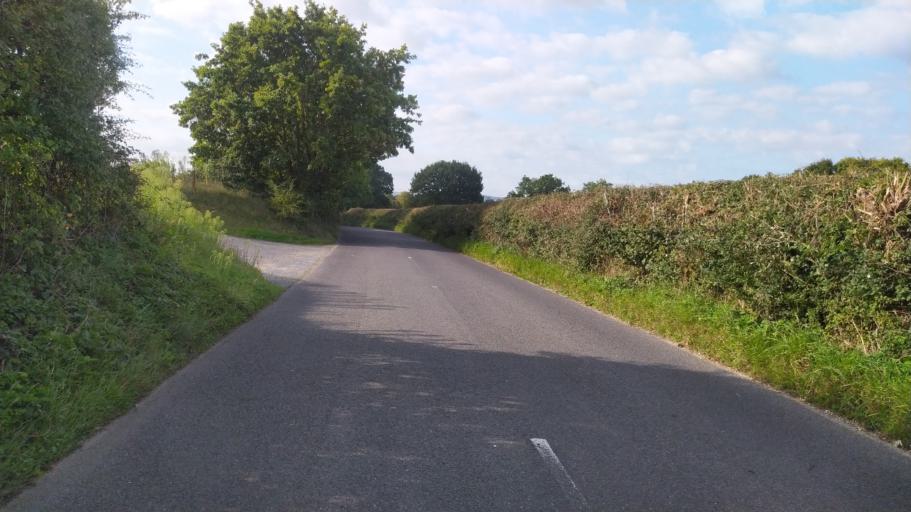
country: GB
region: England
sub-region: Dorset
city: Lytchett Matravers
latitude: 50.7458
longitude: -2.0469
